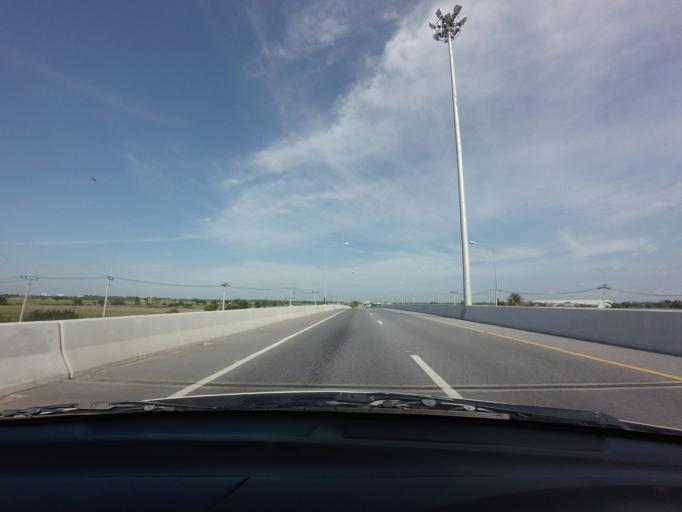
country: TH
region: Suphan Buri
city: Suphan Buri
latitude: 14.4645
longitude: 100.0471
